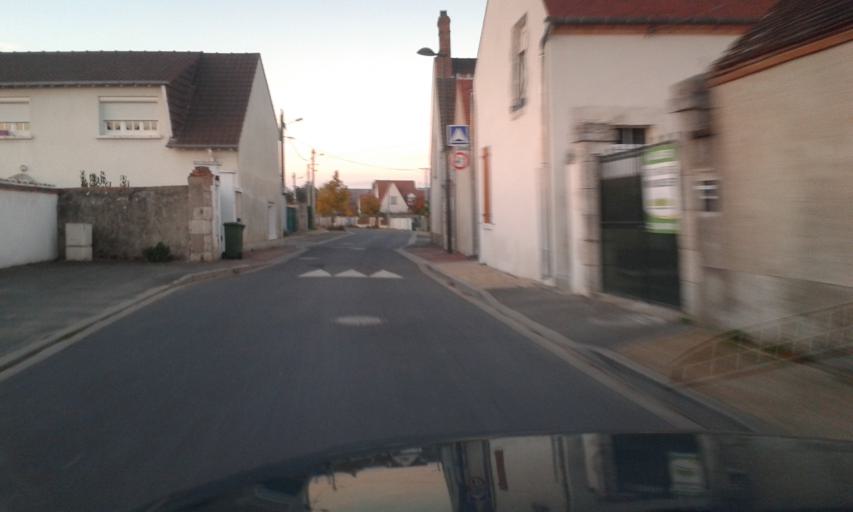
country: FR
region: Centre
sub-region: Departement du Loiret
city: Olivet
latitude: 47.8505
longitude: 1.8829
